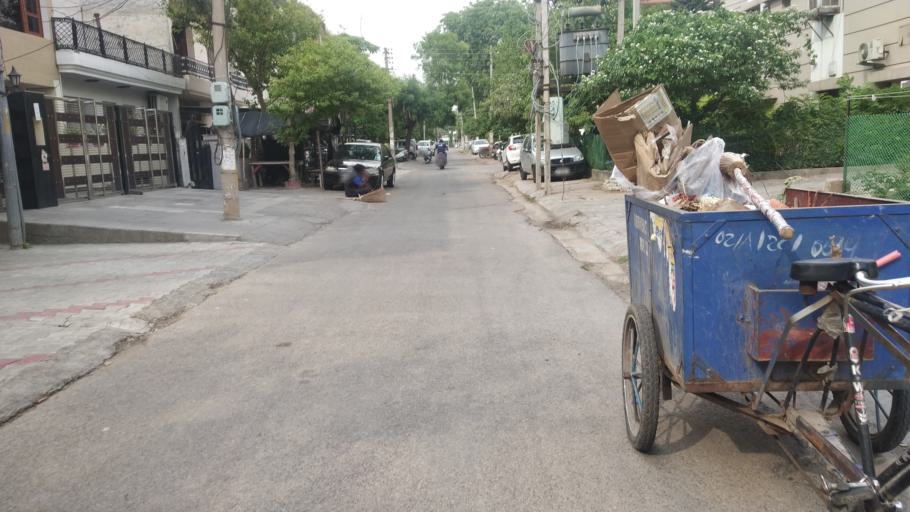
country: IN
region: Punjab
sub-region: Ajitgarh
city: Mohali
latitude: 30.7062
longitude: 76.7174
